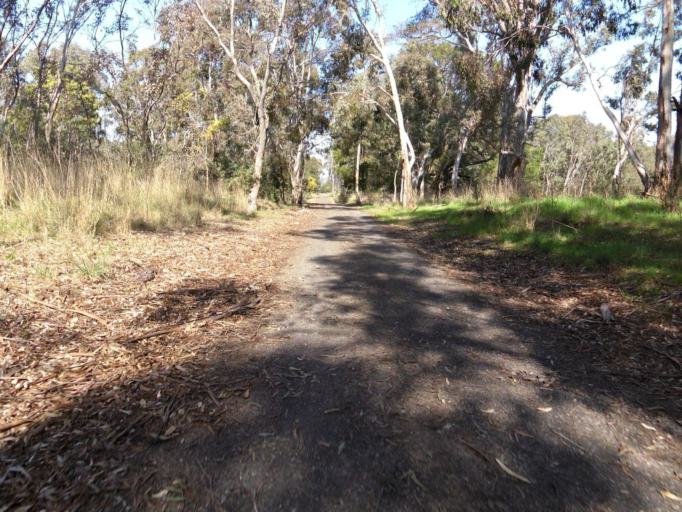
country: AU
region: Victoria
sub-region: Murrindindi
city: Alexandra
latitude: -37.0003
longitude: 145.7452
